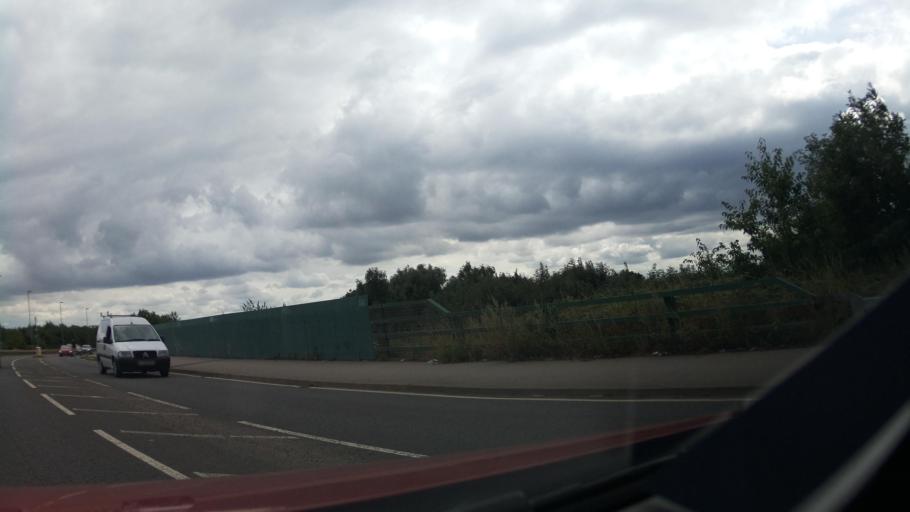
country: GB
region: England
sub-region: Nottinghamshire
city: Burton Joyce
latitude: 52.9751
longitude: -1.0598
